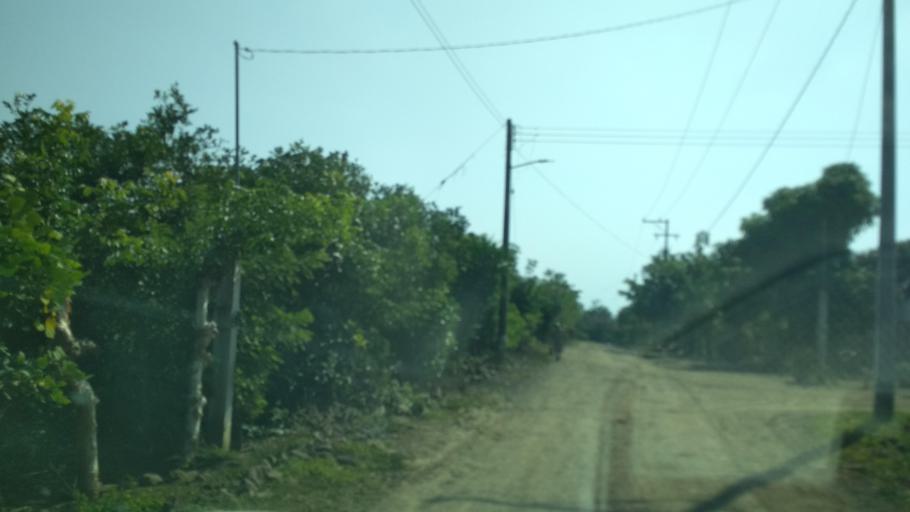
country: MX
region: Puebla
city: San Jose Acateno
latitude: 20.1971
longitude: -97.1852
